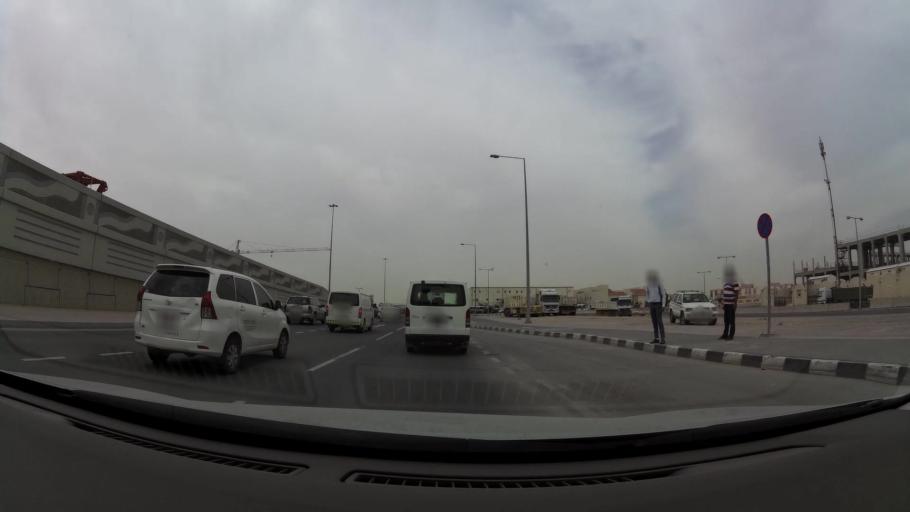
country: QA
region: Baladiyat ar Rayyan
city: Ar Rayyan
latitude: 25.2161
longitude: 51.4391
